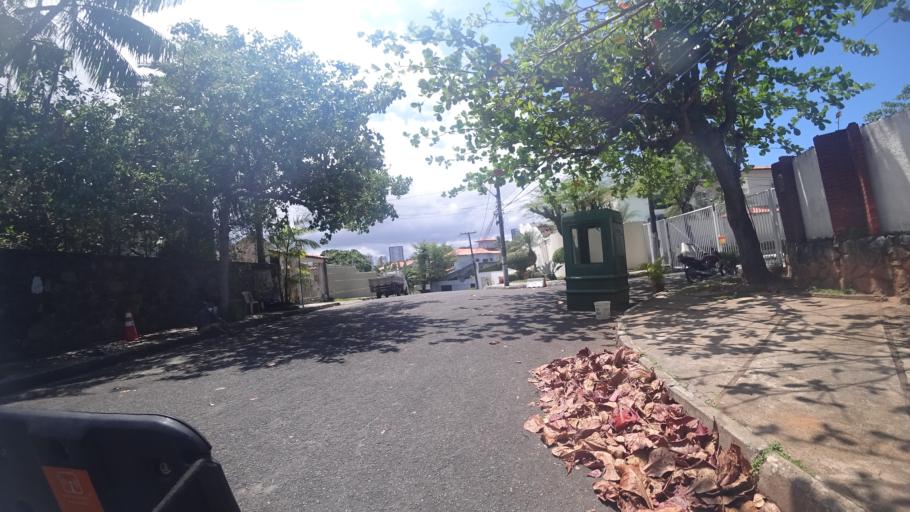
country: BR
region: Bahia
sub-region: Salvador
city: Salvador
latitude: -12.9945
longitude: -38.4695
